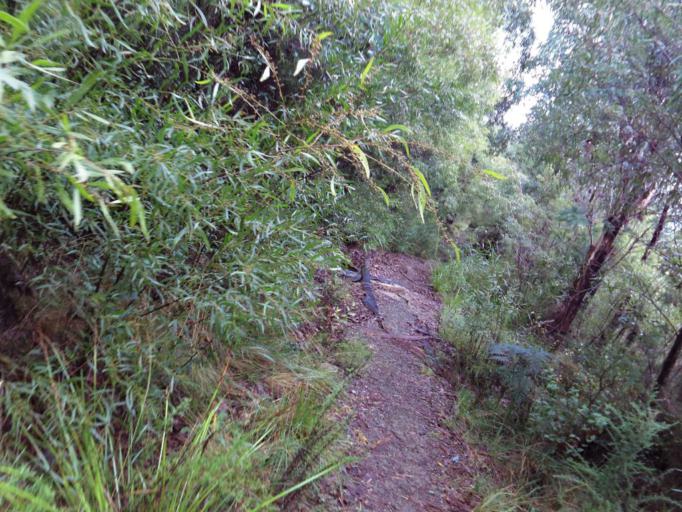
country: AU
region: Victoria
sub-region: Yarra Ranges
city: Millgrove
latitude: -37.5354
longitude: 145.7531
